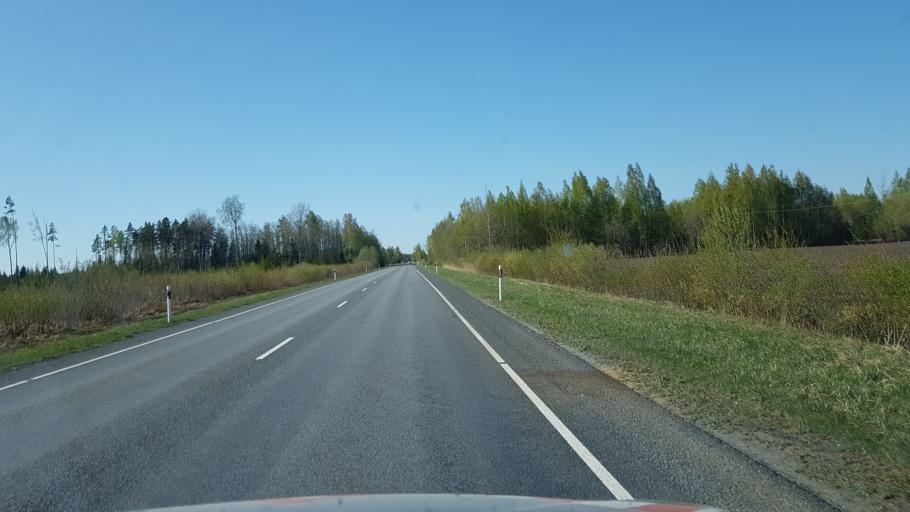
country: EE
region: Paernumaa
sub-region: Paikuse vald
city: Paikuse
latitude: 58.2210
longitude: 24.7069
